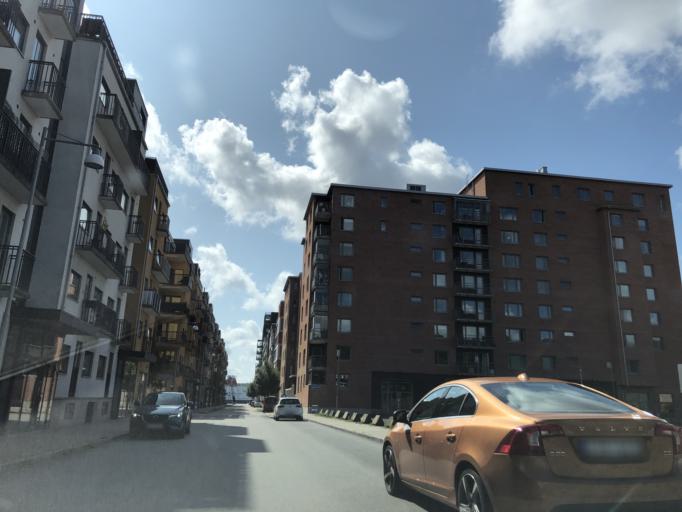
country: SE
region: Vaestra Goetaland
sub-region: Goteborg
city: Majorna
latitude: 57.7009
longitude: 11.9099
